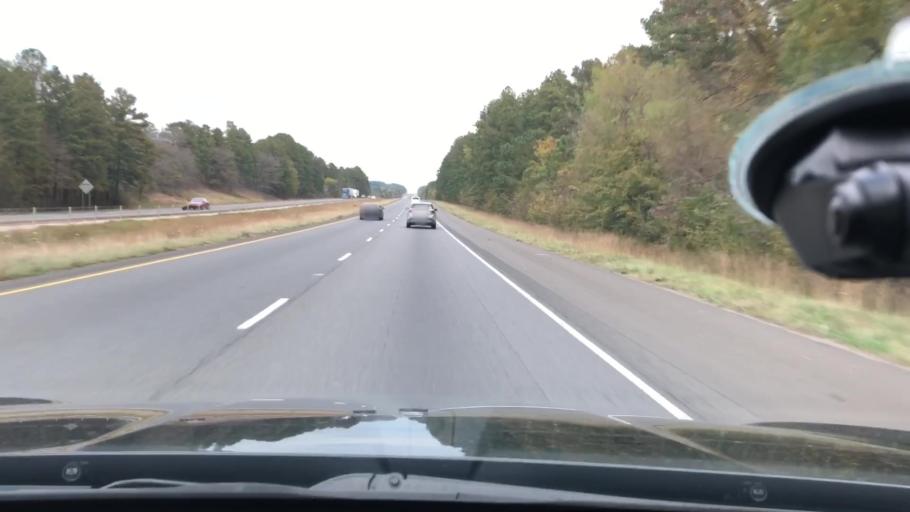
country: US
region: Arkansas
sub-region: Clark County
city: Arkadelphia
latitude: 34.2529
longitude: -92.9891
